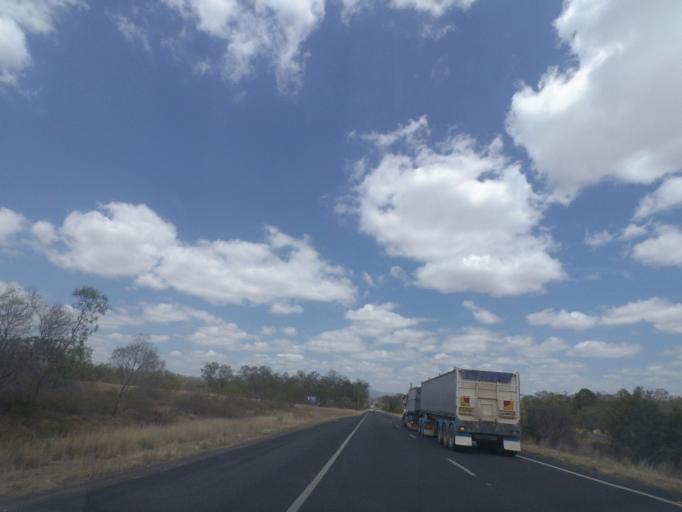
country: AU
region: Queensland
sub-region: Lockyer Valley
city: Gatton
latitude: -27.5520
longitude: 152.1529
